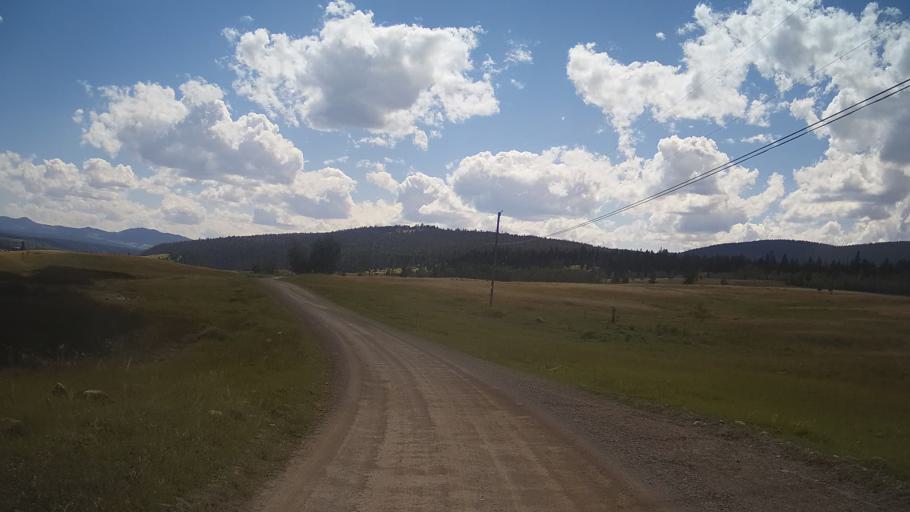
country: CA
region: British Columbia
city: Lillooet
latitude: 51.3172
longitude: -121.9819
